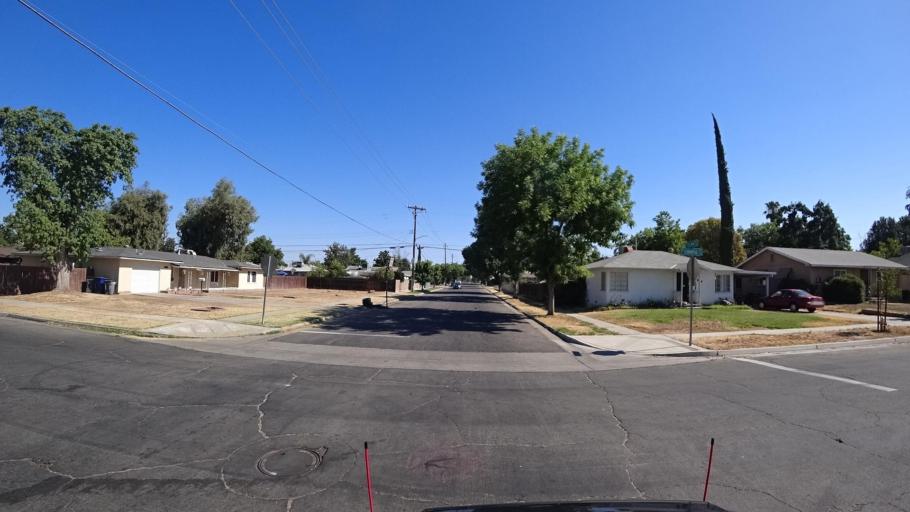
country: US
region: California
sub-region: Fresno County
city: Fresno
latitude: 36.7774
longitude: -119.8221
